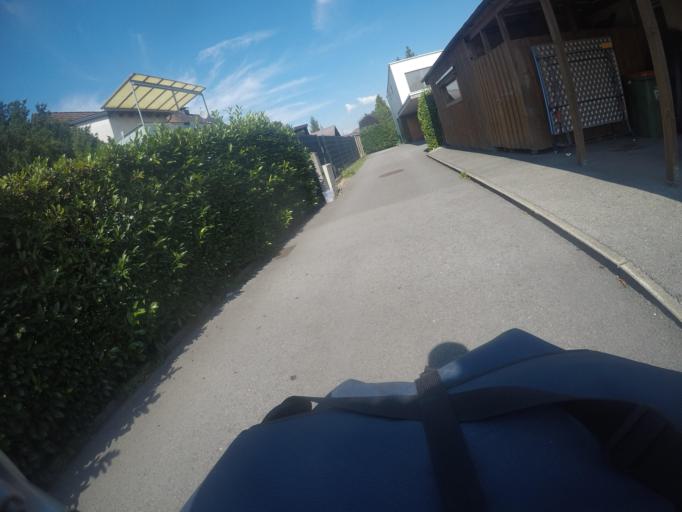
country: AT
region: Vorarlberg
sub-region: Politischer Bezirk Dornbirn
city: Lustenau
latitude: 47.4326
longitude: 9.6728
